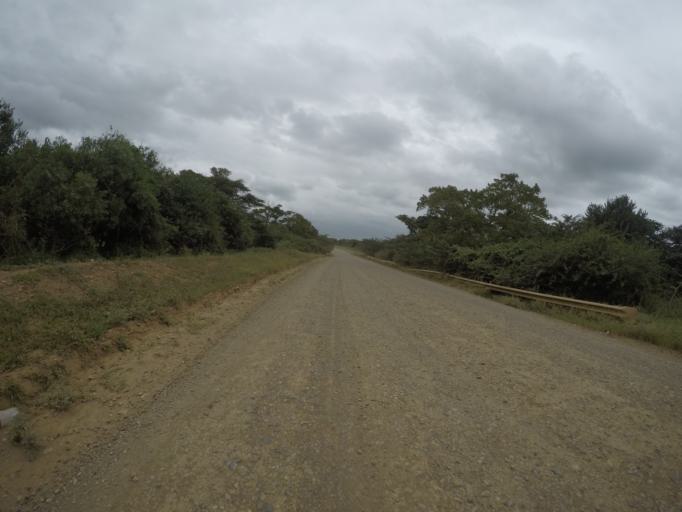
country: ZA
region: KwaZulu-Natal
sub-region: uThungulu District Municipality
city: Empangeni
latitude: -28.5887
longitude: 31.8433
